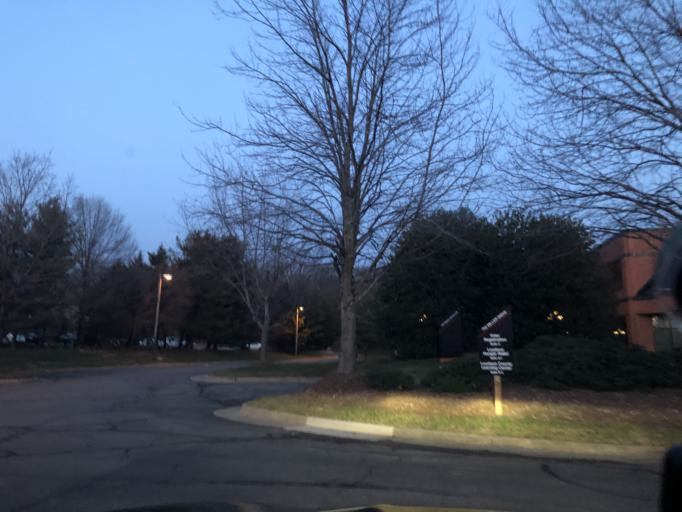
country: US
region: Virginia
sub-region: Loudoun County
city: Leesburg
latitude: 39.0833
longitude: -77.5559
